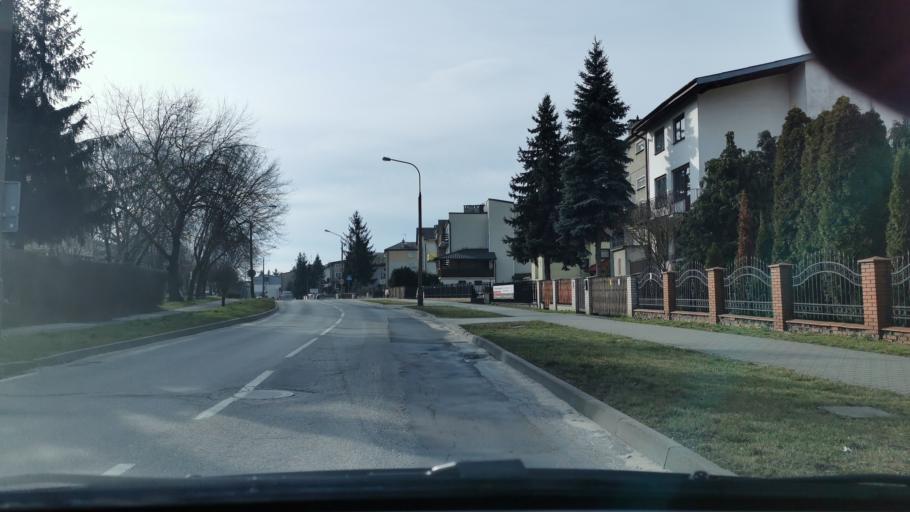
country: PL
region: Lublin Voivodeship
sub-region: Powiat lubelski
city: Lublin
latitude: 51.2089
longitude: 22.5415
